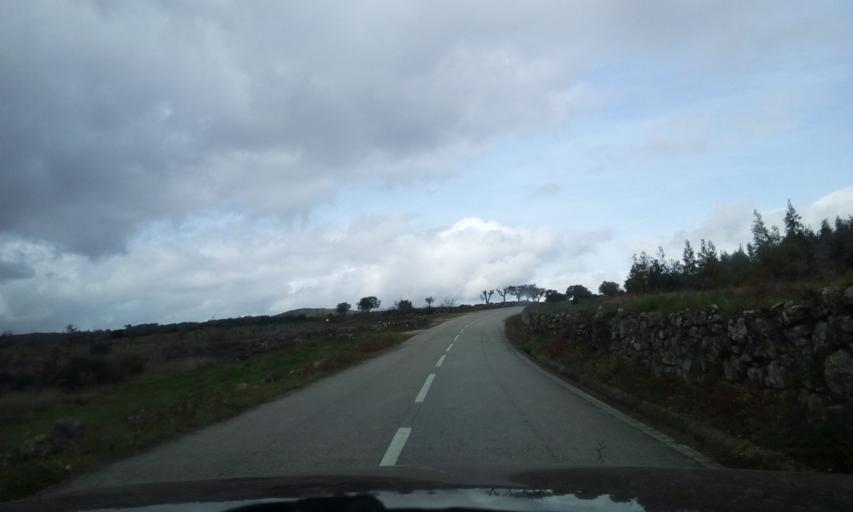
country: PT
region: Guarda
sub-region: Fornos de Algodres
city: Fornos de Algodres
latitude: 40.6587
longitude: -7.5915
